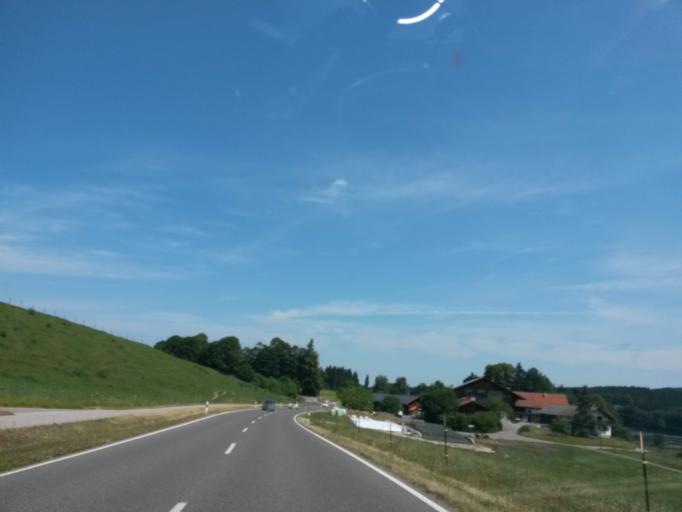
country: DE
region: Bavaria
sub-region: Upper Bavaria
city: Steingaden
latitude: 47.6798
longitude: 10.8581
